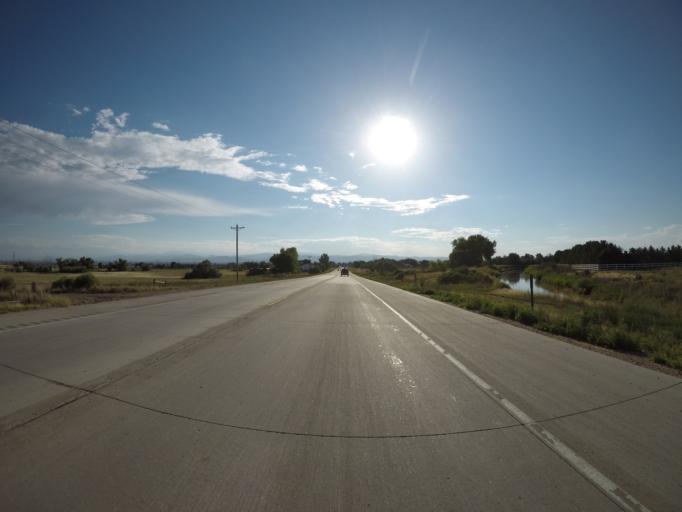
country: US
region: Colorado
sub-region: Weld County
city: Severance
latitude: 40.5816
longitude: -104.9168
